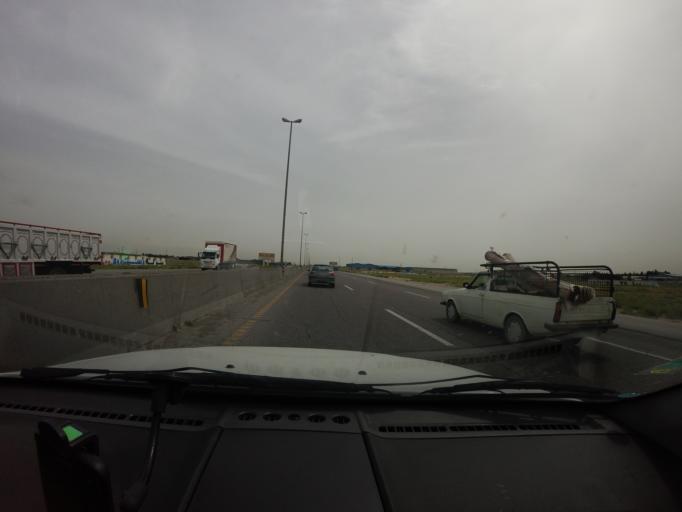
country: IR
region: Tehran
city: Robat Karim
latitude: 35.5384
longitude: 51.1076
